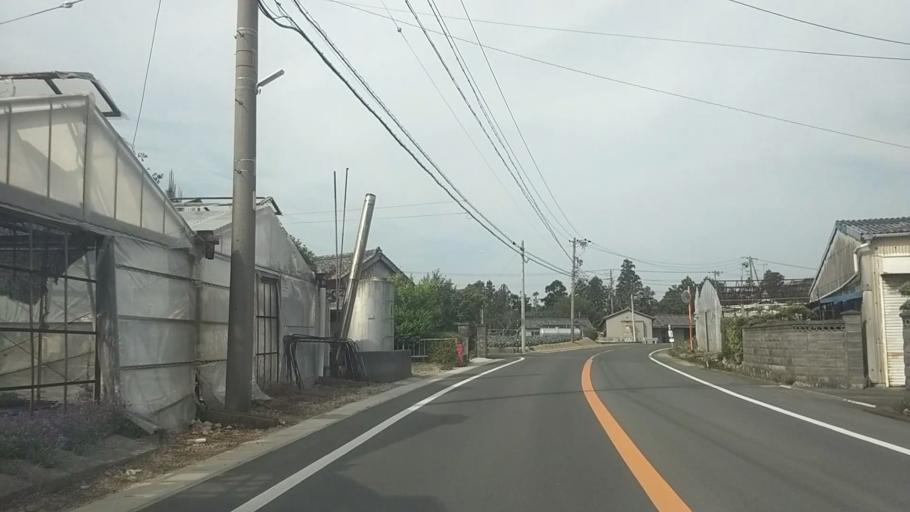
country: JP
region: Shizuoka
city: Hamamatsu
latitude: 34.7130
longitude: 137.6430
